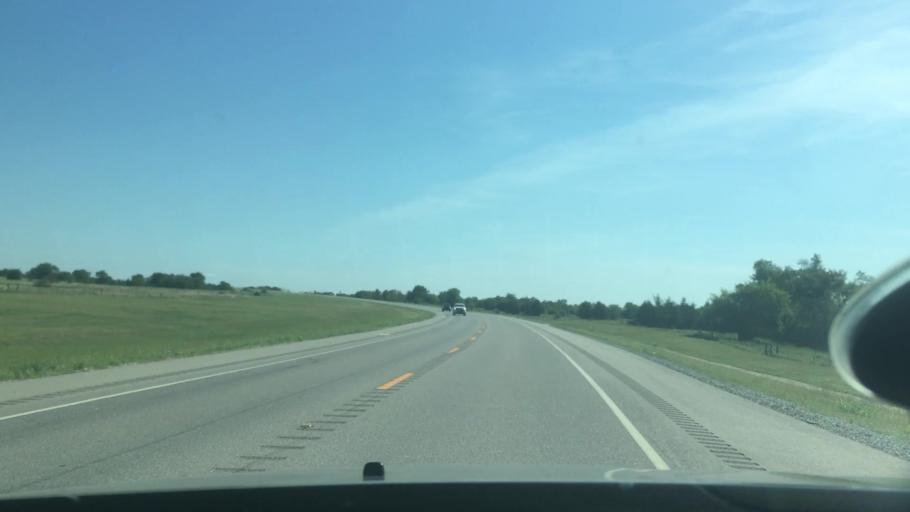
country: US
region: Oklahoma
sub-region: Bryan County
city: Durant
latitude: 33.9680
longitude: -96.3454
